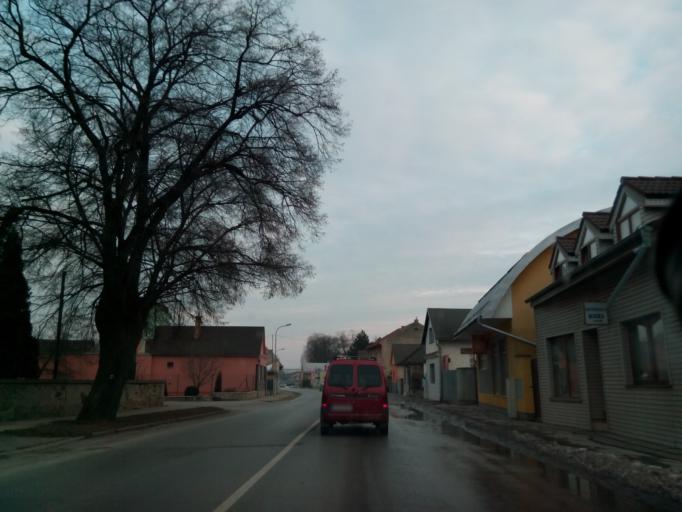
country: SK
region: Presovsky
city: Sabinov
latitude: 49.1054
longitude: 21.0892
